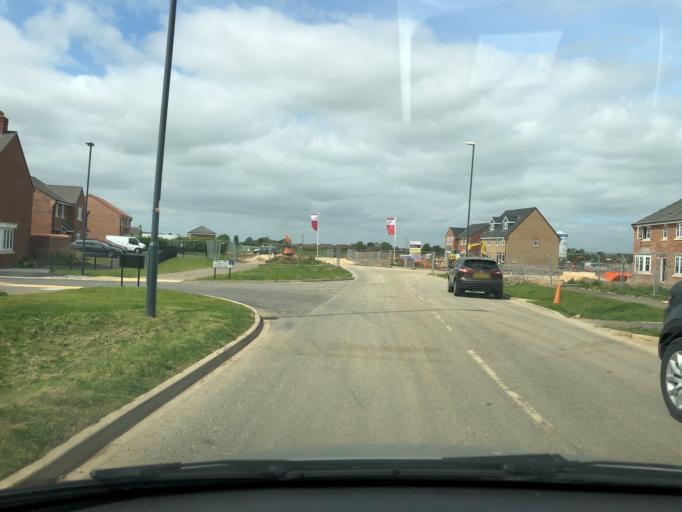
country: GB
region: England
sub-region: North Yorkshire
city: Thirsk
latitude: 54.2212
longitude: -1.3545
